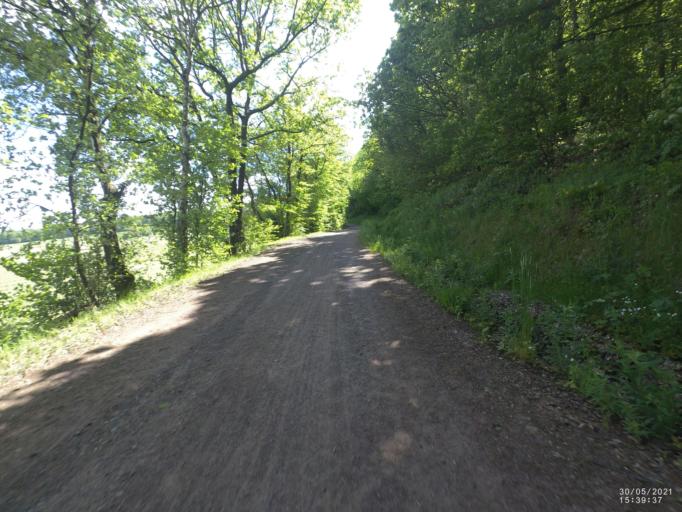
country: DE
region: Rheinland-Pfalz
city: Waldesch
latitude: 50.2717
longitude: 7.5496
